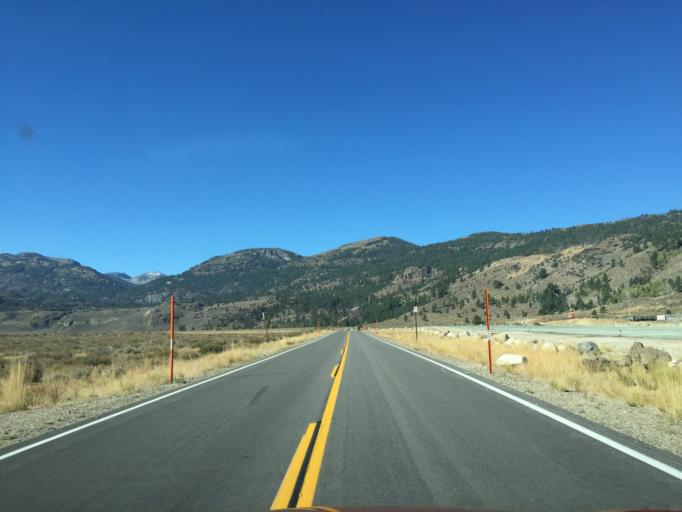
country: US
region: California
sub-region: Mono County
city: Bridgeport
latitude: 38.3551
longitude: -119.5187
